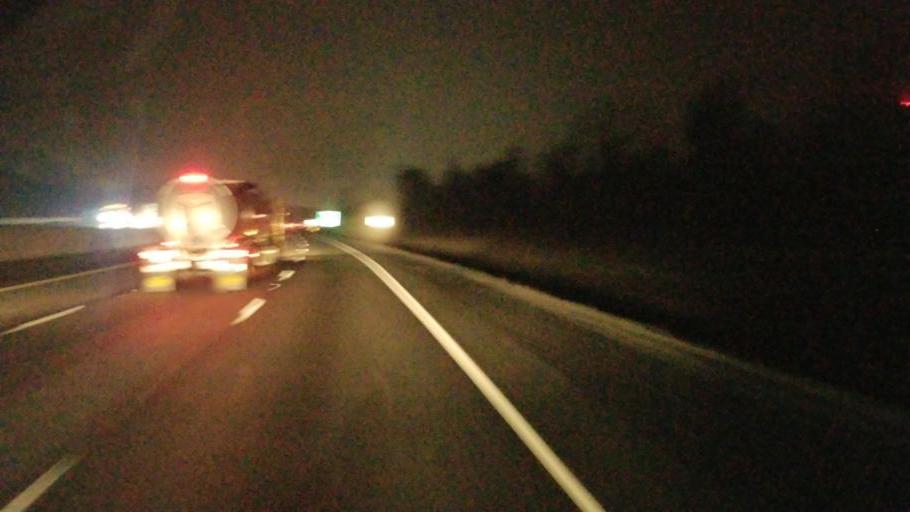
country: US
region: Indiana
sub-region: Marion County
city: Meridian Hills
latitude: 39.9289
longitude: -86.1765
